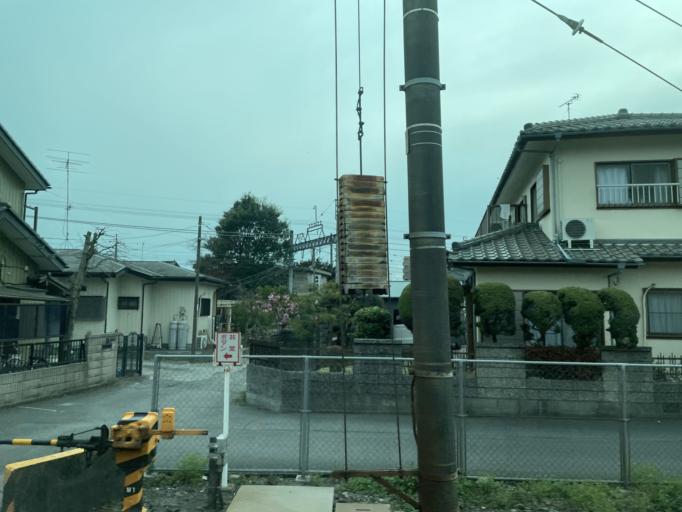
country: JP
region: Saitama
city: Kasukabe
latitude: 35.9820
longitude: 139.7484
